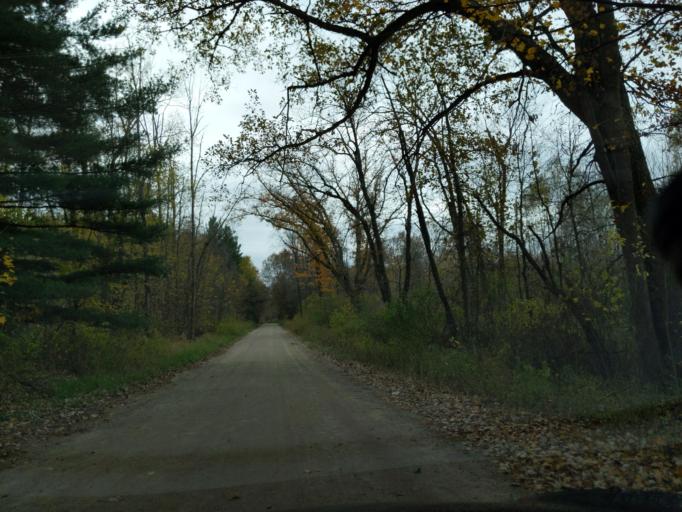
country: US
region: Michigan
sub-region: Eaton County
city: Eaton Rapids
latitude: 42.5496
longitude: -84.6154
